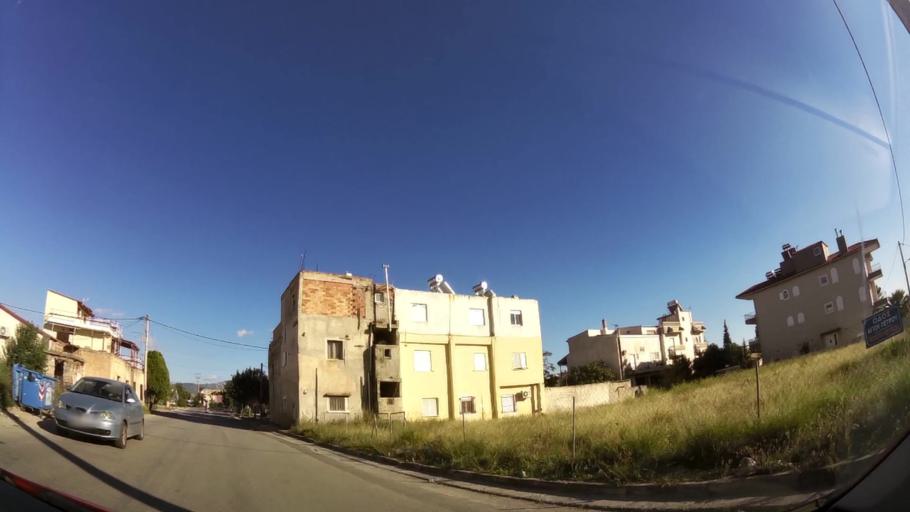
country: GR
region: Attica
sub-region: Nomarchia Anatolikis Attikis
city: Acharnes
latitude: 38.0951
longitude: 23.7301
